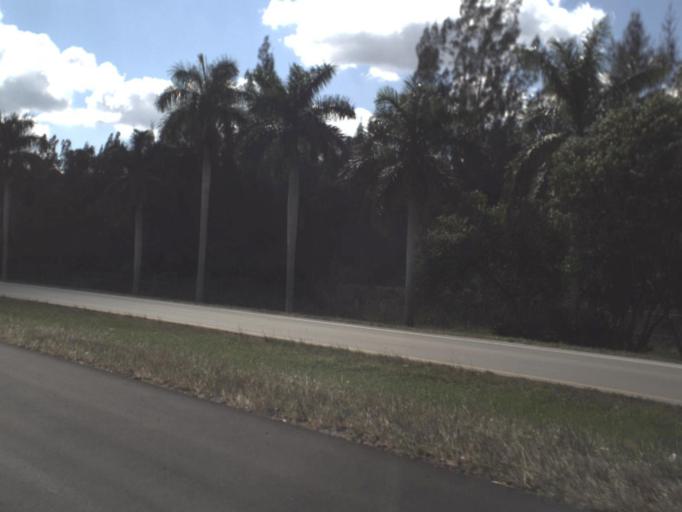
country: US
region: Florida
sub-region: Broward County
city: Weston
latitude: 26.1433
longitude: -80.3435
